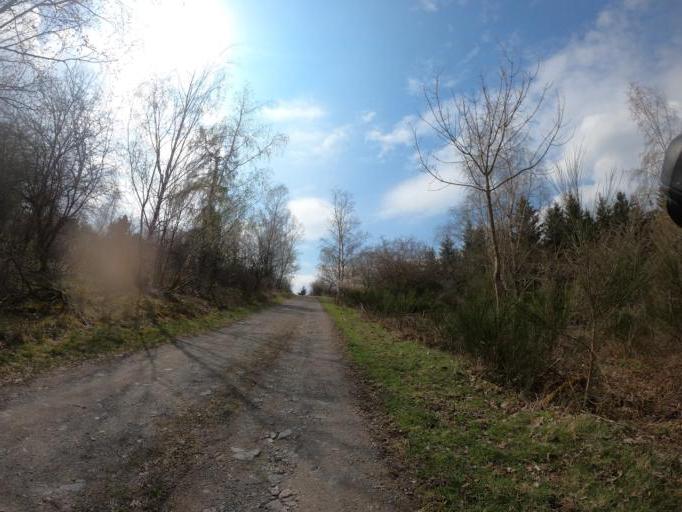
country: DE
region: North Rhine-Westphalia
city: Heimbach
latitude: 50.5928
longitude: 6.3909
